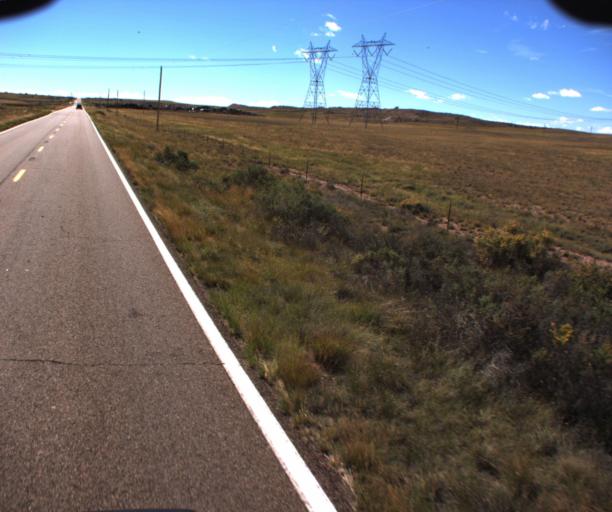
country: US
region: Arizona
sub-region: Apache County
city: Saint Johns
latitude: 34.5790
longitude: -109.3339
